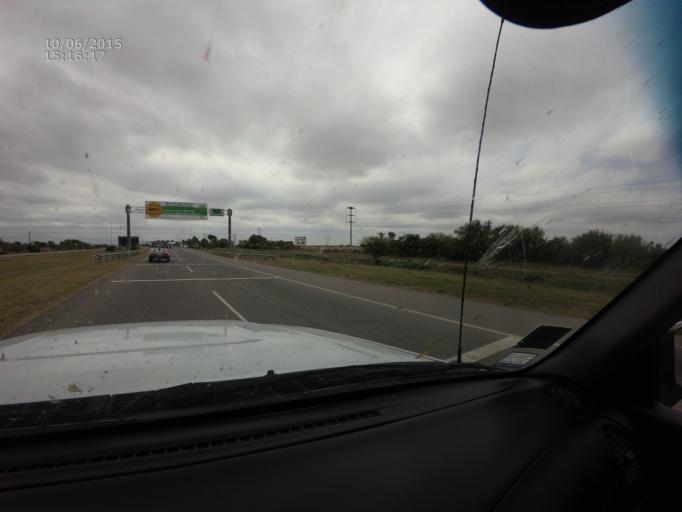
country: AR
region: Cordoba
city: Toledo
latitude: -31.5423
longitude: -63.9696
